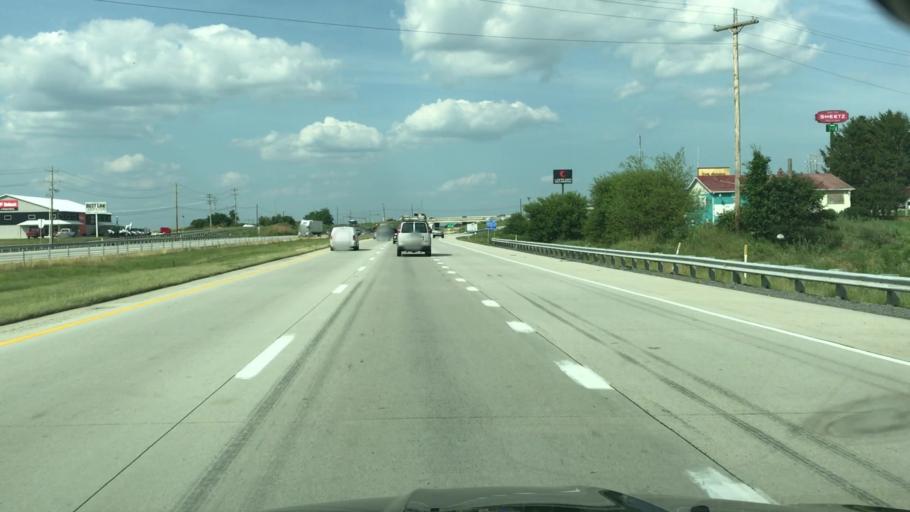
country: US
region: Pennsylvania
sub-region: Cumberland County
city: Shippensburg
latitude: 40.0121
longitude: -77.5382
